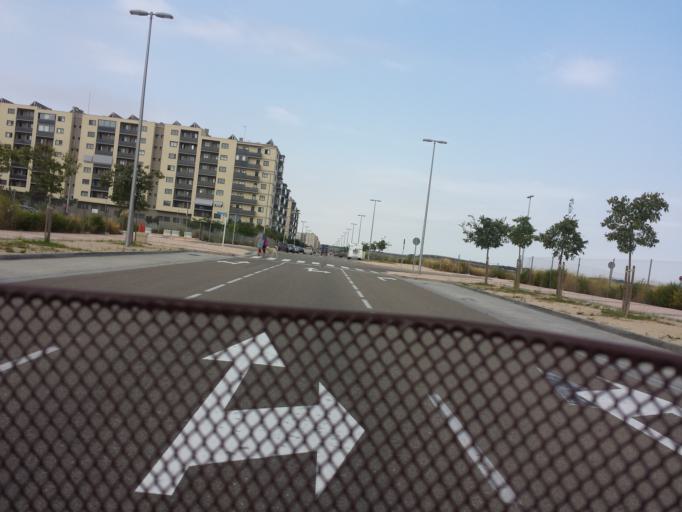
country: ES
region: Aragon
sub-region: Provincia de Zaragoza
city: Montecanal
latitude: 41.6232
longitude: -0.9500
